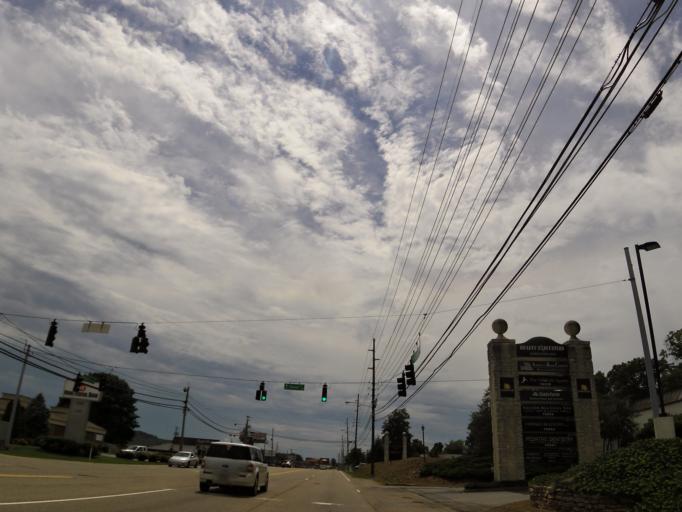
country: US
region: Tennessee
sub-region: Knox County
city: Farragut
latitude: 35.9002
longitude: -84.1258
